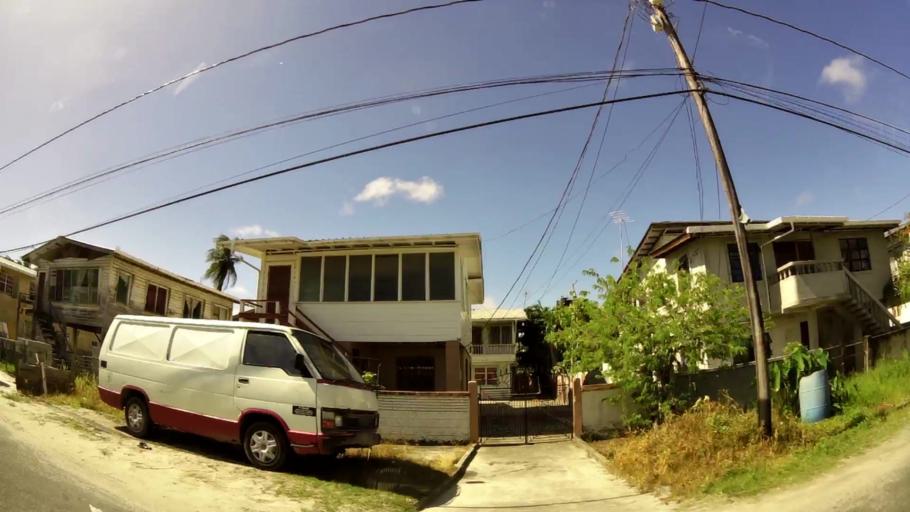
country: GY
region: Demerara-Mahaica
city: Georgetown
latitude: 6.8090
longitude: -58.1364
